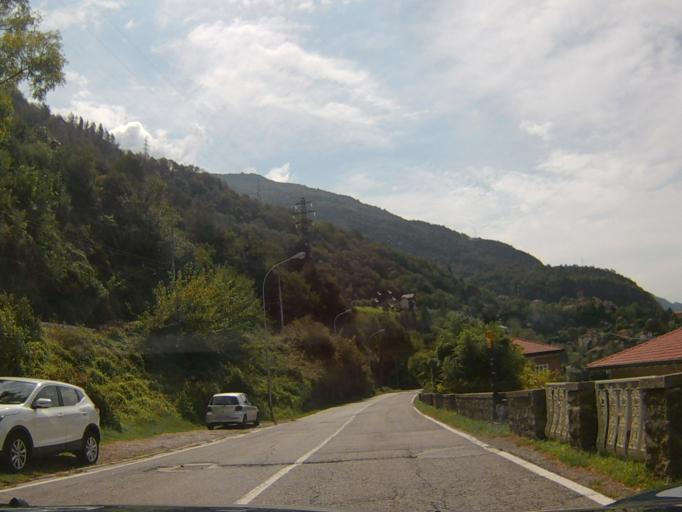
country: IT
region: Lombardy
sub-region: Provincia di Lecco
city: Dervio
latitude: 46.0853
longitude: 9.3106
